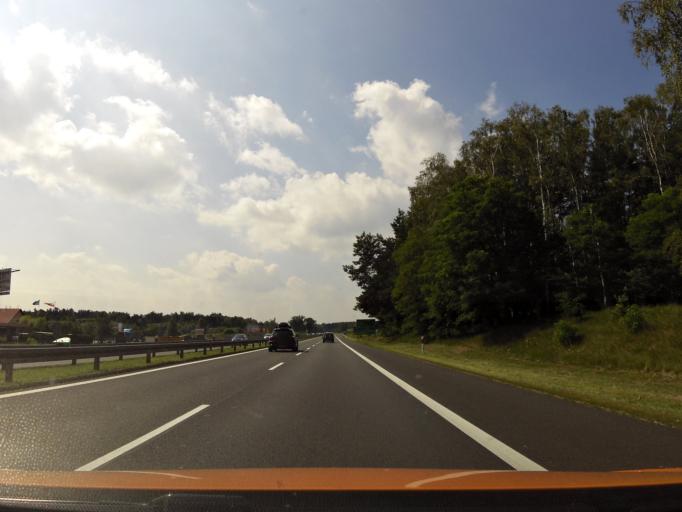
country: PL
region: West Pomeranian Voivodeship
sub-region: Powiat goleniowski
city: Goleniow
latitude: 53.5817
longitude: 14.8115
